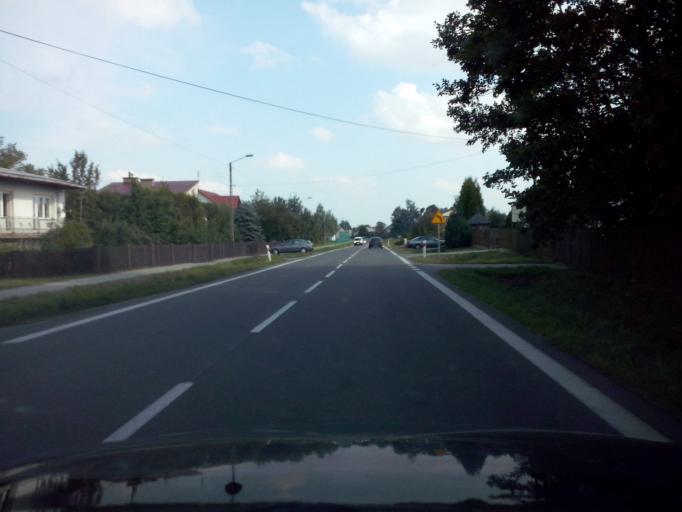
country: PL
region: Subcarpathian Voivodeship
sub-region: Powiat kolbuszowski
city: Niwiska
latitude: 50.2608
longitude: 21.6677
